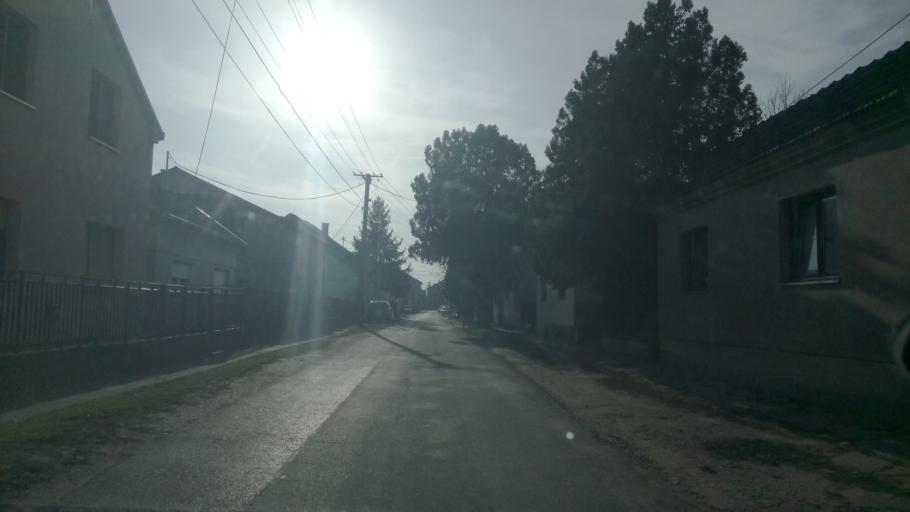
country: RS
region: Autonomna Pokrajina Vojvodina
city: Nova Pazova
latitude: 44.9496
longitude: 20.2220
